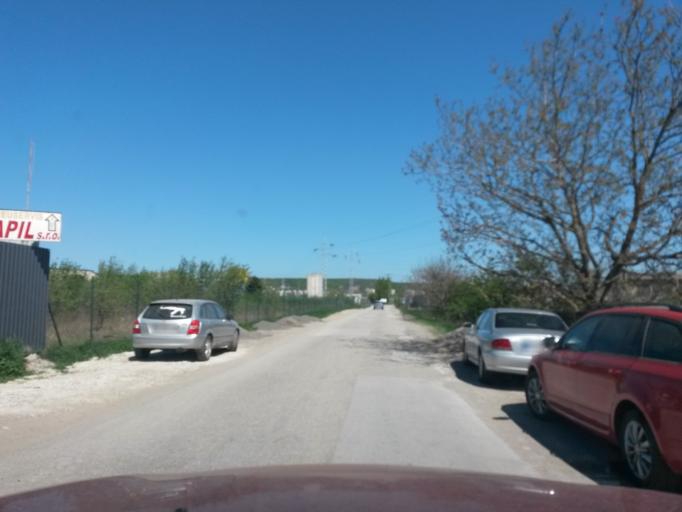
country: SK
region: Kosicky
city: Kosice
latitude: 48.6721
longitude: 21.2724
